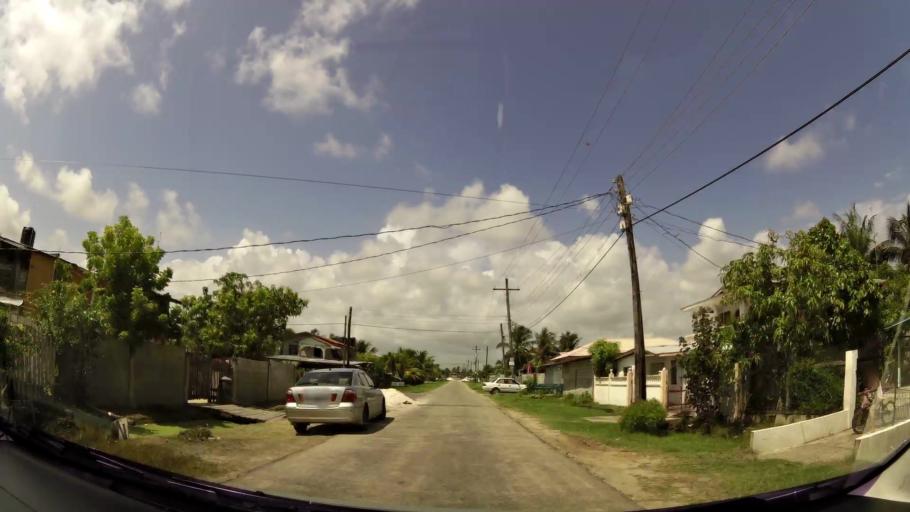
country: GY
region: Demerara-Mahaica
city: Mahaica Village
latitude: 6.7750
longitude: -58.0130
